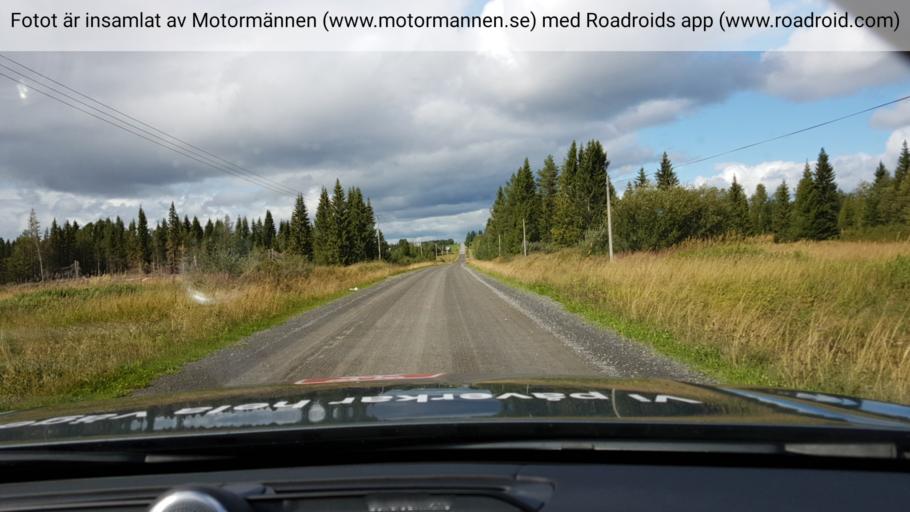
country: SE
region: Jaemtland
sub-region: OEstersunds Kommun
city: Lit
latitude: 63.6335
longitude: 14.9654
